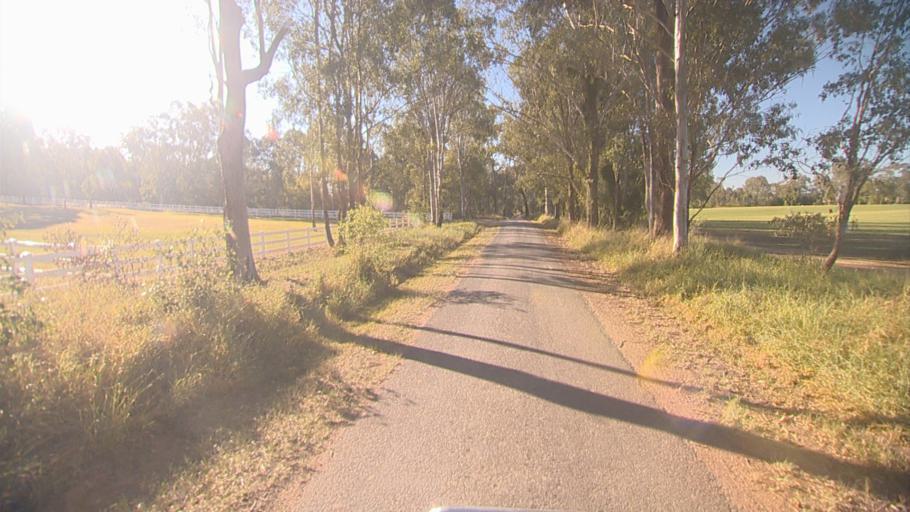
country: AU
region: Queensland
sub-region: Logan
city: North Maclean
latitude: -27.7758
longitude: 153.0379
